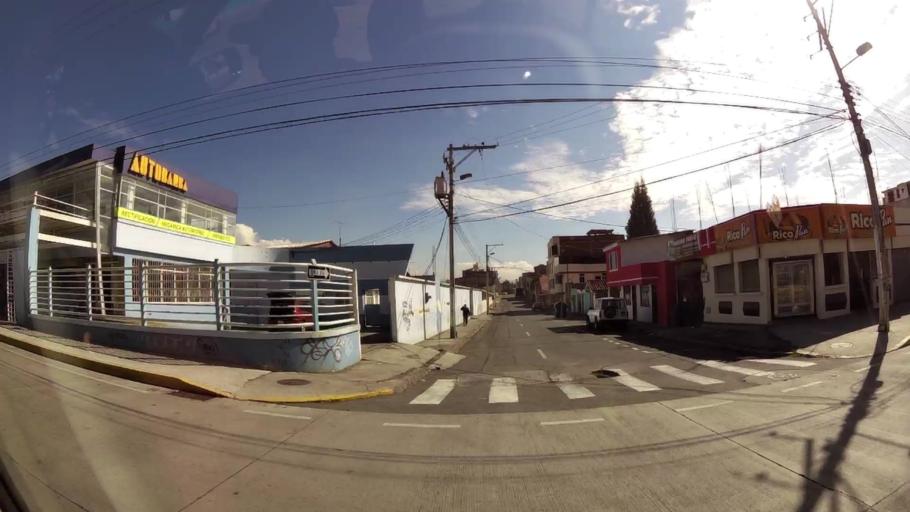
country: EC
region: Chimborazo
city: Riobamba
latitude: -1.6539
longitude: -78.6664
